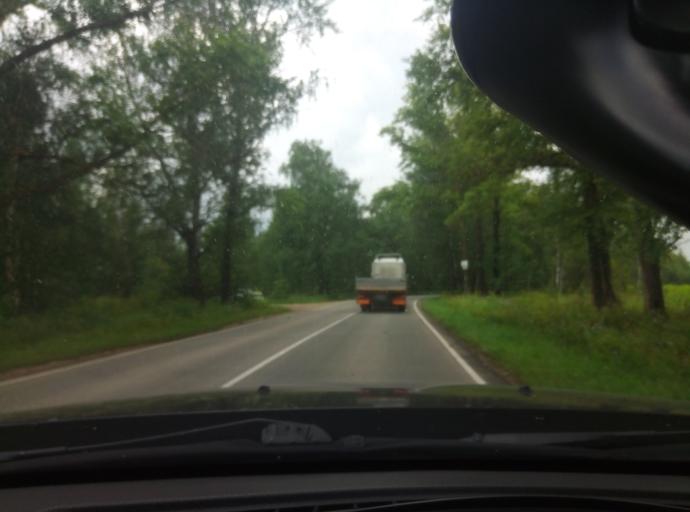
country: RU
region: Tula
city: Priupskiy
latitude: 53.9651
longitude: 37.7205
